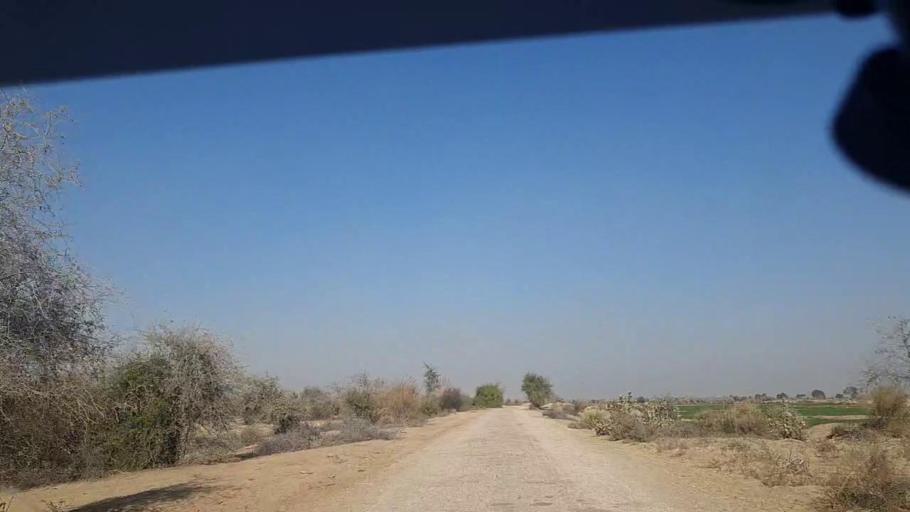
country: PK
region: Sindh
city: Khanpur
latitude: 27.5634
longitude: 69.3374
